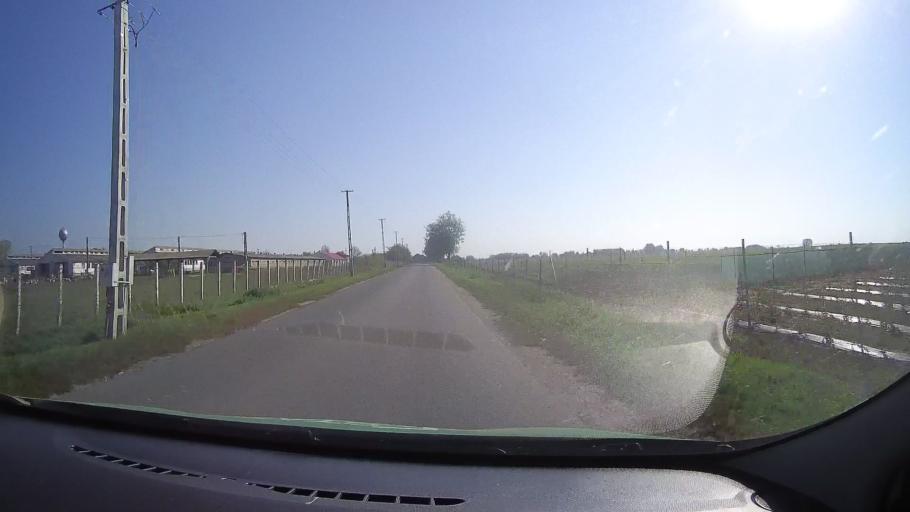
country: RO
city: Foieni
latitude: 47.6959
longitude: 22.3659
